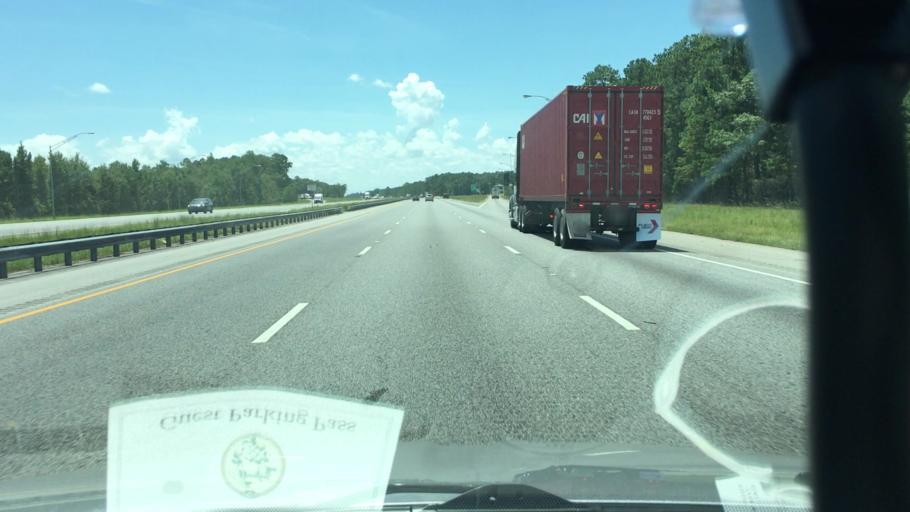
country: US
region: Georgia
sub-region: McIntosh County
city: Darien
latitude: 31.4846
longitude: -81.4473
